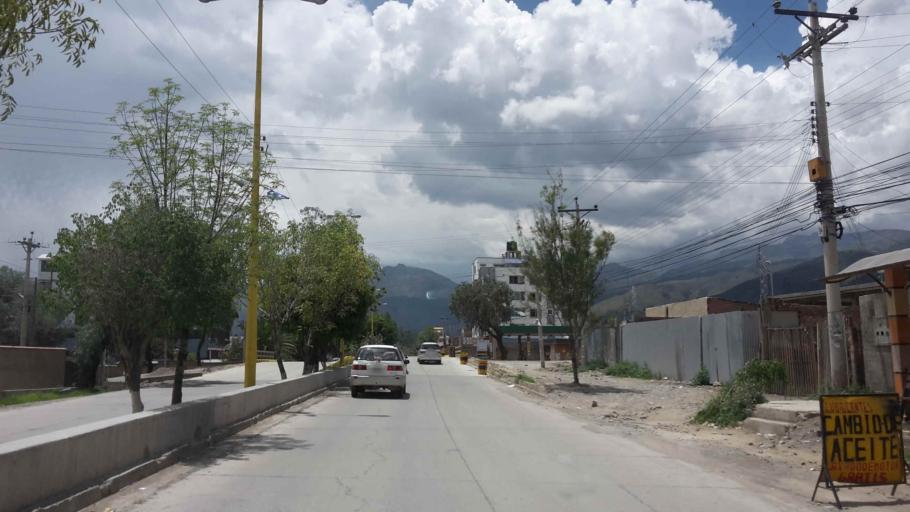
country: BO
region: Cochabamba
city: Cochabamba
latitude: -17.3473
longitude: -66.1988
